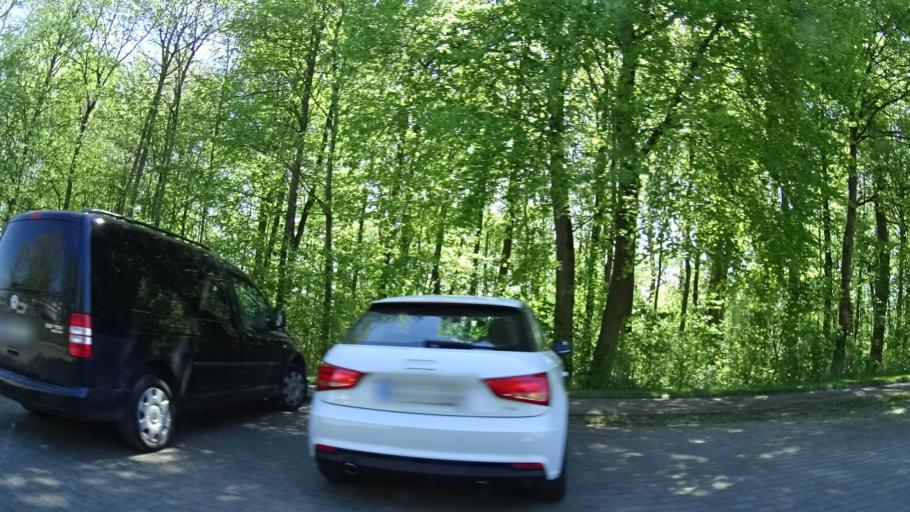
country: DE
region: Baden-Wuerttemberg
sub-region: Freiburg Region
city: Rottweil
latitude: 48.1573
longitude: 8.6241
